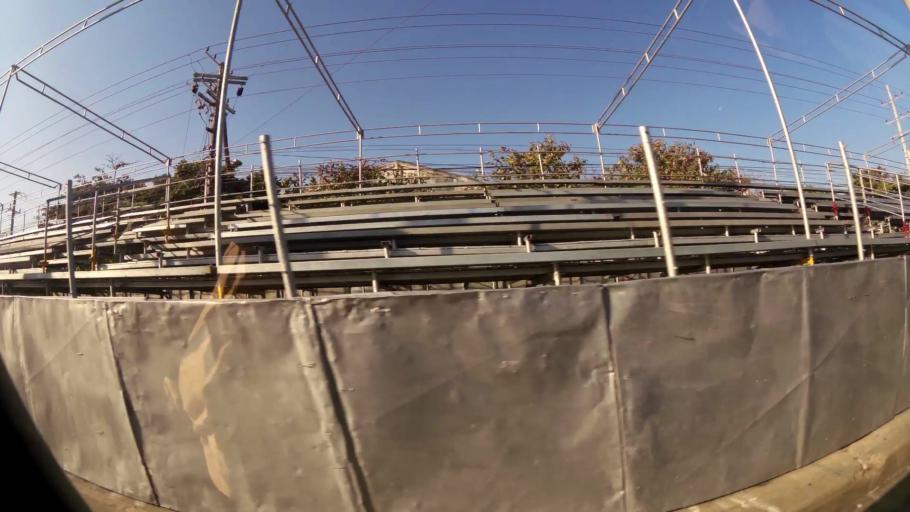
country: CO
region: Atlantico
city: Barranquilla
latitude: 11.0233
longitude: -74.8010
